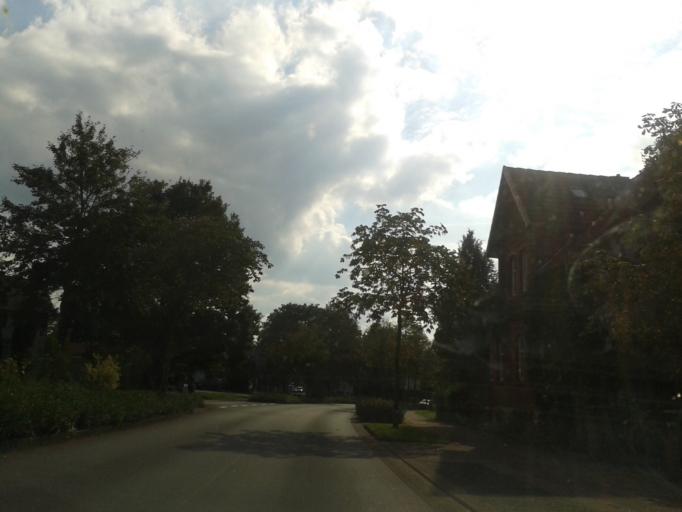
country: DE
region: North Rhine-Westphalia
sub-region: Regierungsbezirk Detmold
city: Schlangen
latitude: 51.8125
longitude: 8.8477
